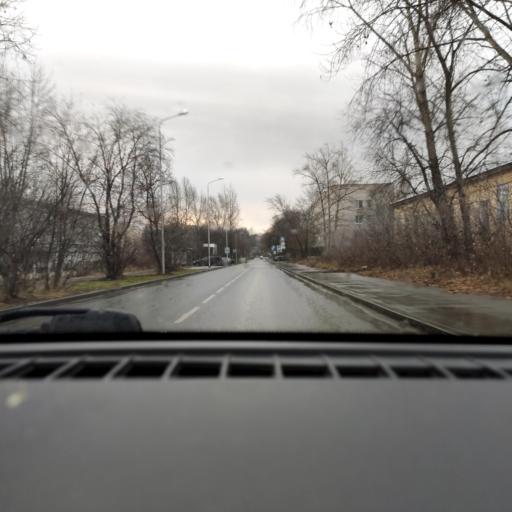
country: RU
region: Perm
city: Kultayevo
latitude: 57.9949
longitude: 55.9355
